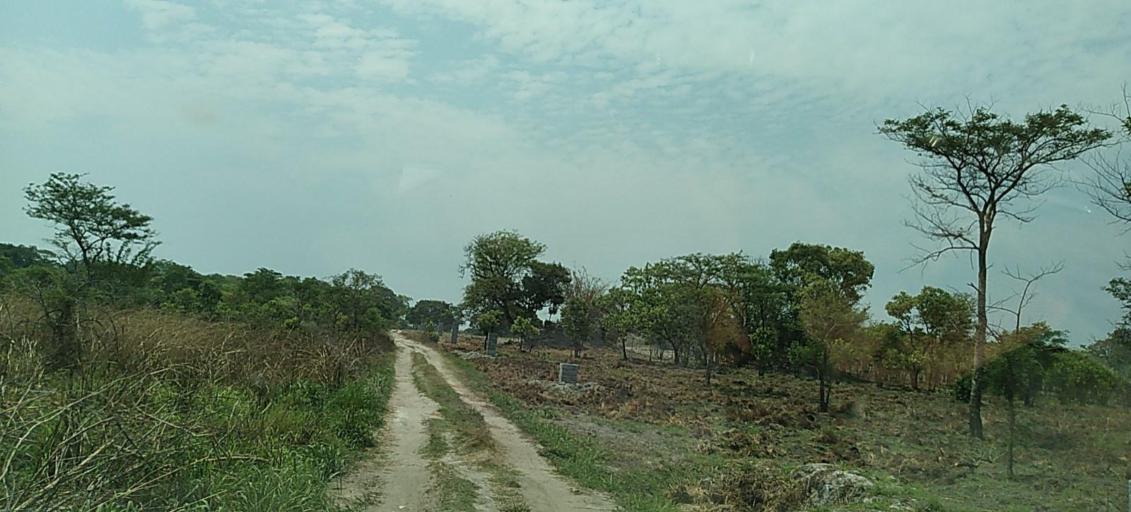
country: ZM
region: Copperbelt
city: Kalulushi
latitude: -12.9369
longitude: 28.1142
